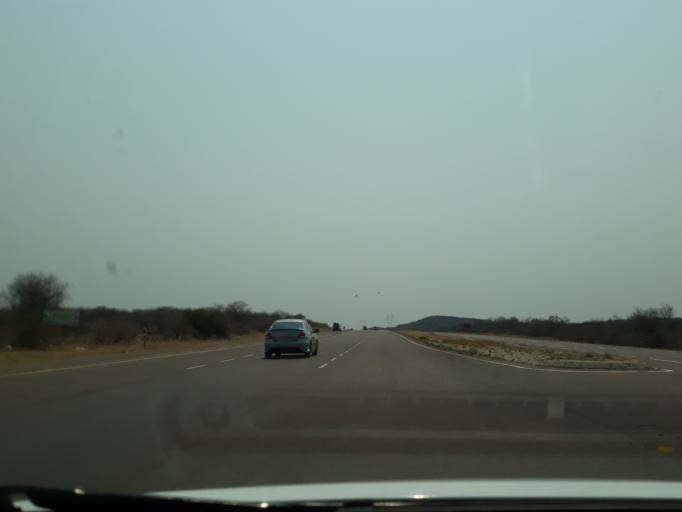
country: BW
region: Kgatleng
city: Bokaa
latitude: -24.4025
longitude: 26.0558
